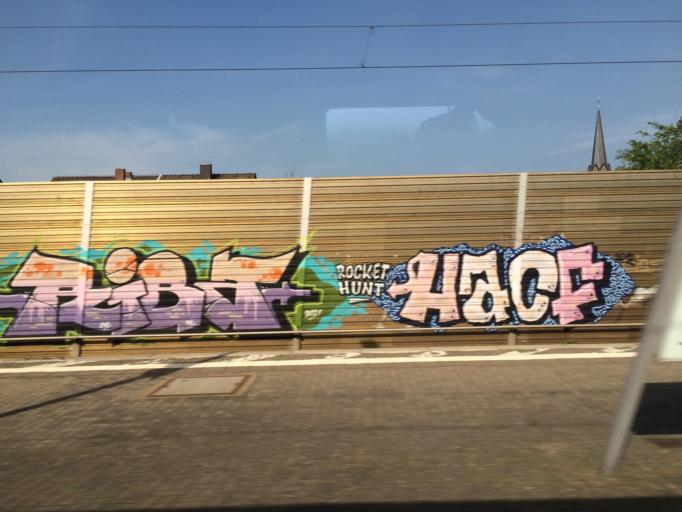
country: DE
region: North Rhine-Westphalia
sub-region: Regierungsbezirk Koln
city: Wahn-Heide
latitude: 50.8271
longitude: 7.1143
